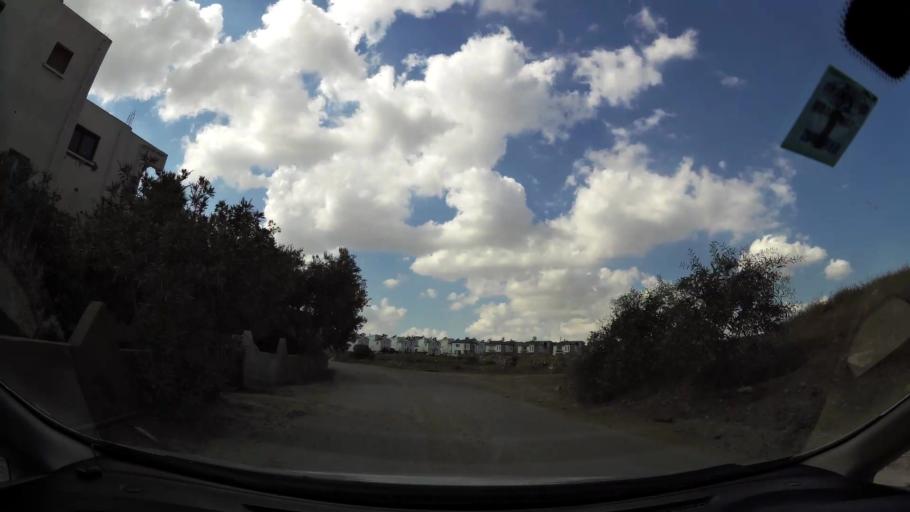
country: CY
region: Lefkosia
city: Nicosia
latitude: 35.2207
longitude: 33.3741
